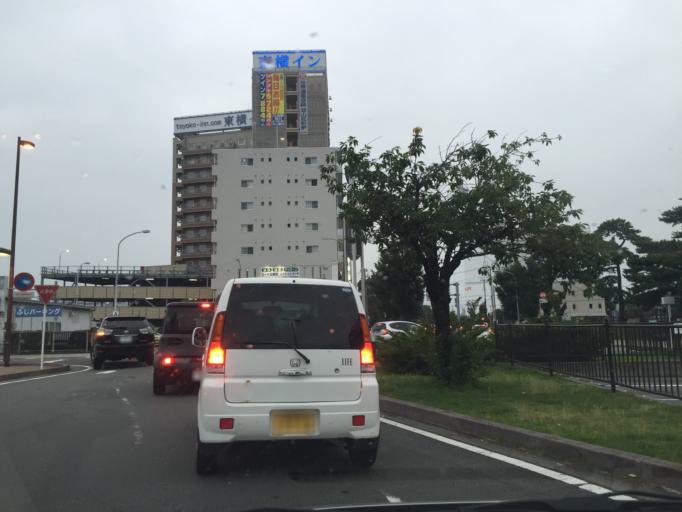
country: JP
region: Shizuoka
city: Mishima
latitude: 35.1276
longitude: 138.9108
